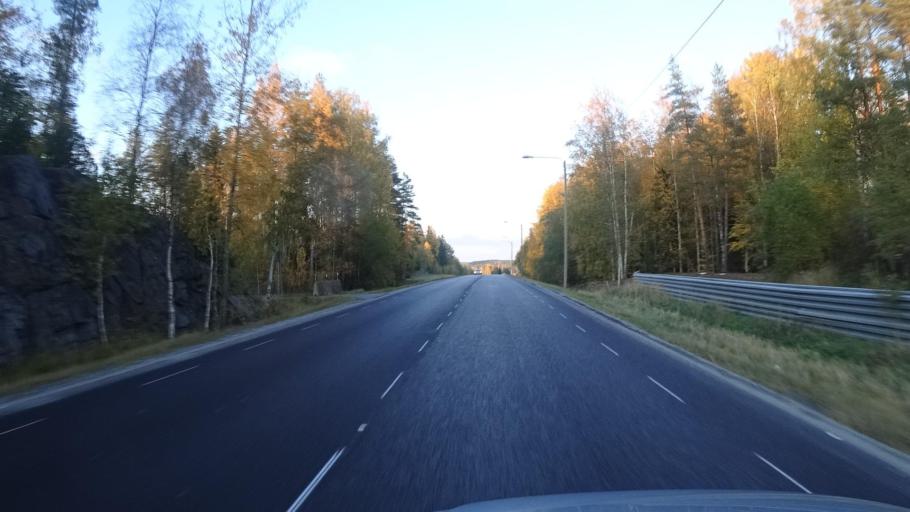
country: FI
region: Haeme
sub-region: Forssa
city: Jokioinen
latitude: 60.8164
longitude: 23.5438
